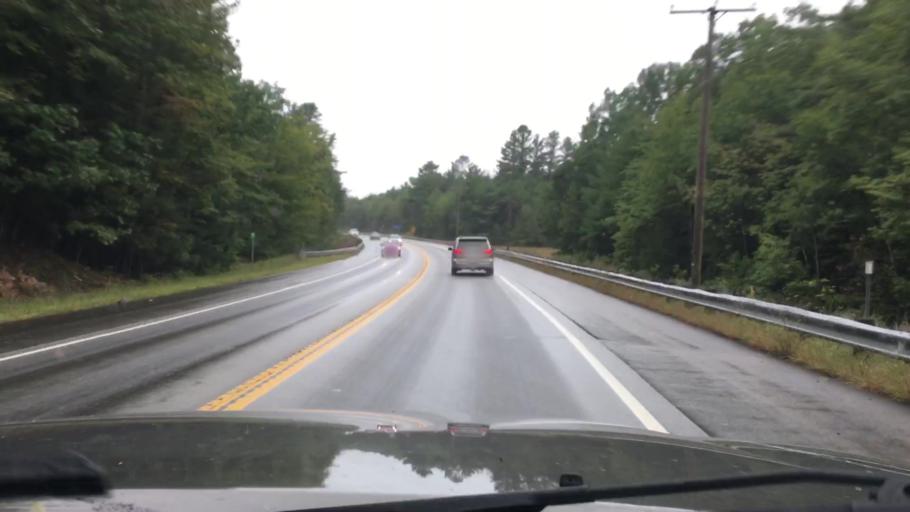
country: US
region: New Hampshire
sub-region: Cheshire County
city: Keene
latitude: 42.9301
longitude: -72.3248
